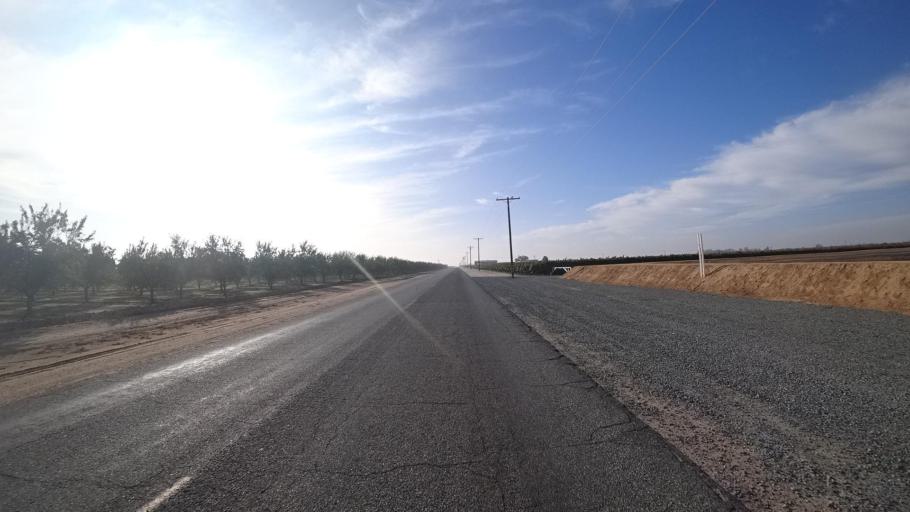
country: US
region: California
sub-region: Kern County
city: McFarland
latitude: 35.6860
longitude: -119.2048
